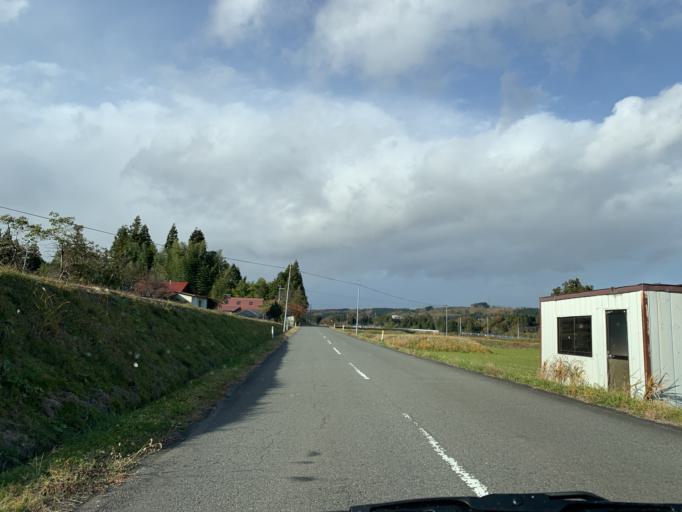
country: JP
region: Iwate
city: Ichinoseki
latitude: 39.0227
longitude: 141.0742
